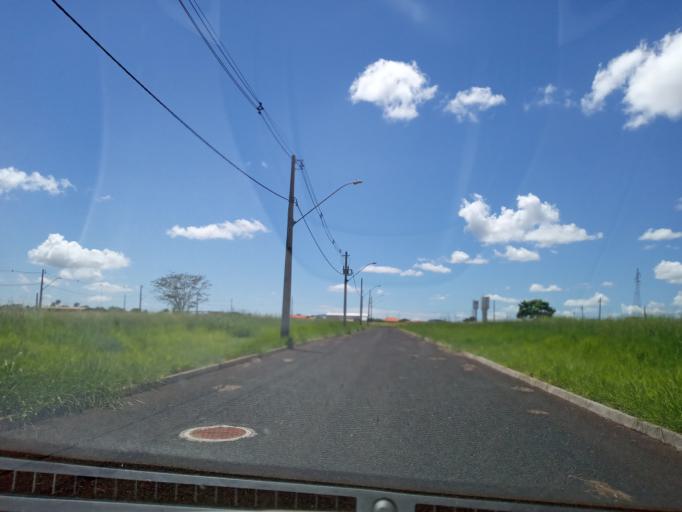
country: BR
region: Minas Gerais
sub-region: Centralina
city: Centralina
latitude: -18.5994
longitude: -49.1985
